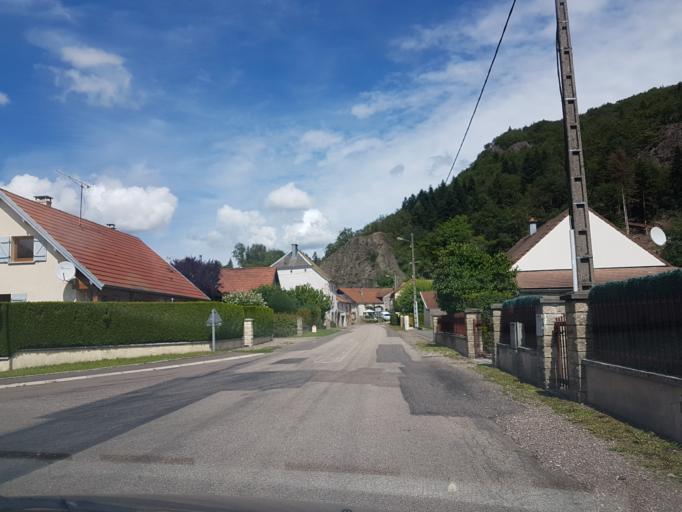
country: FR
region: Franche-Comte
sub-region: Departement de la Haute-Saone
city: Melisey
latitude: 47.8387
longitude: 6.5631
